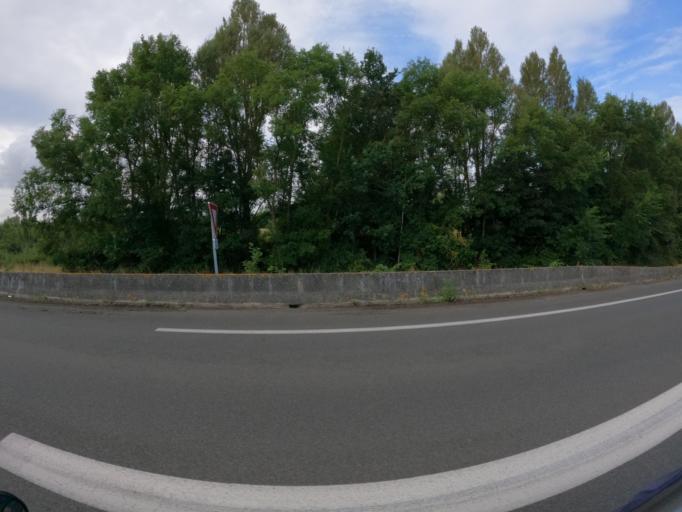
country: FR
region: Centre
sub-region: Departement d'Indre-et-Loire
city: Bourgueil
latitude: 47.2594
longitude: 0.1459
